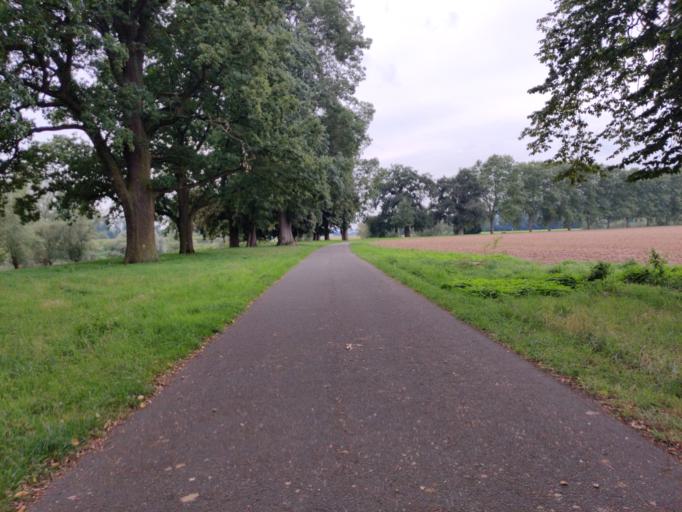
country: DE
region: North Rhine-Westphalia
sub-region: Regierungsbezirk Detmold
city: Hoexter
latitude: 51.7737
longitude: 9.4106
